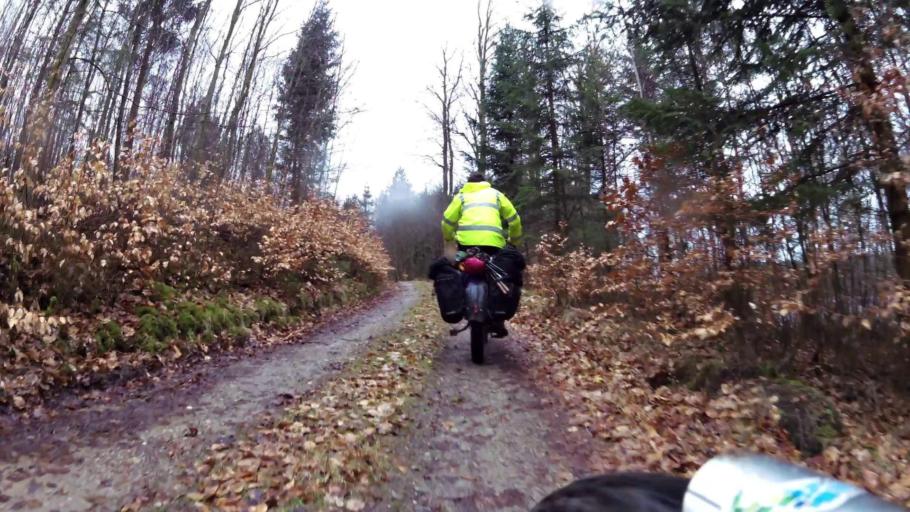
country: PL
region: Pomeranian Voivodeship
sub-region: Powiat bytowski
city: Miastko
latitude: 54.0472
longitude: 17.0622
